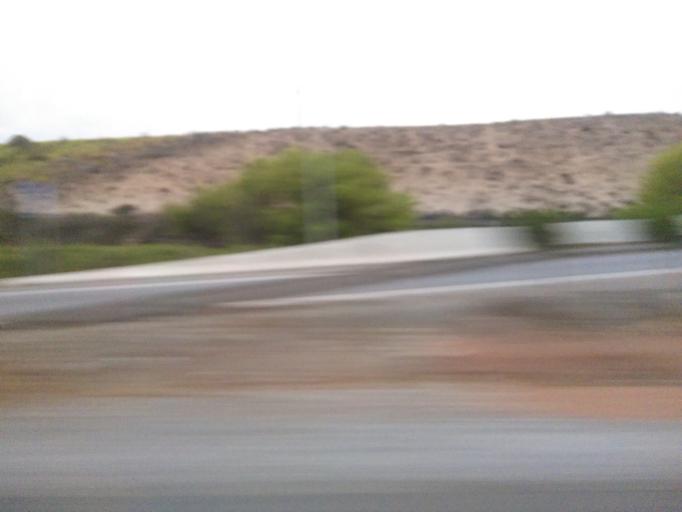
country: CL
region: Coquimbo
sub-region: Provincia de Elqui
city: La Serena
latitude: -29.8409
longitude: -71.2588
